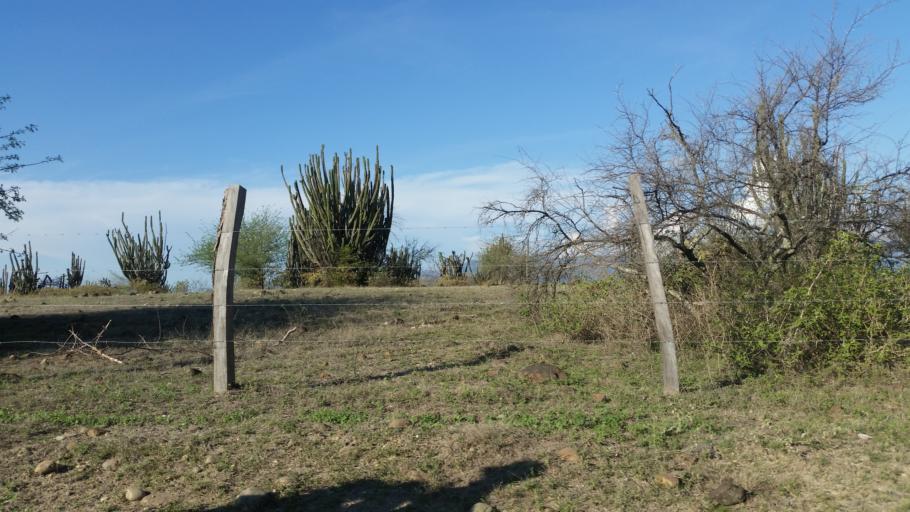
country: CO
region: Huila
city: Villavieja
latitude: 3.2304
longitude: -75.1525
